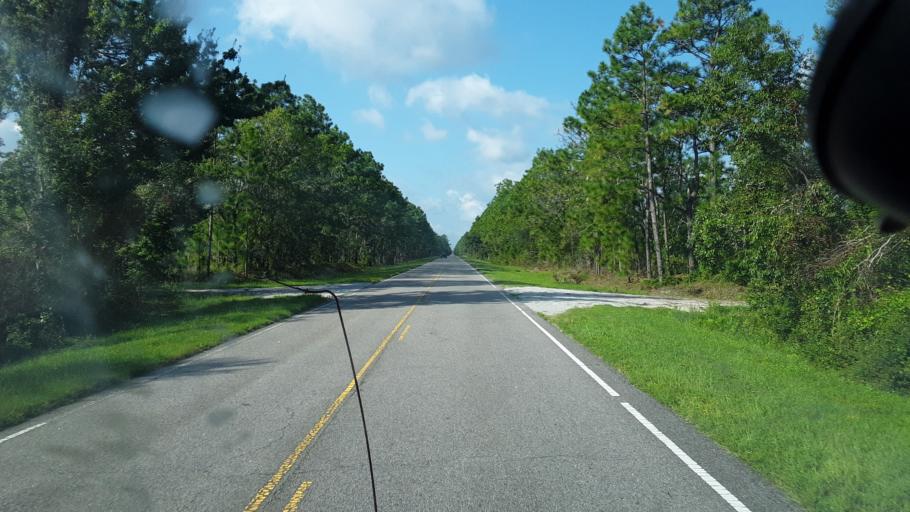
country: US
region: North Carolina
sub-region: Brunswick County
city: Boiling Spring Lakes
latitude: 34.0478
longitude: -77.9991
